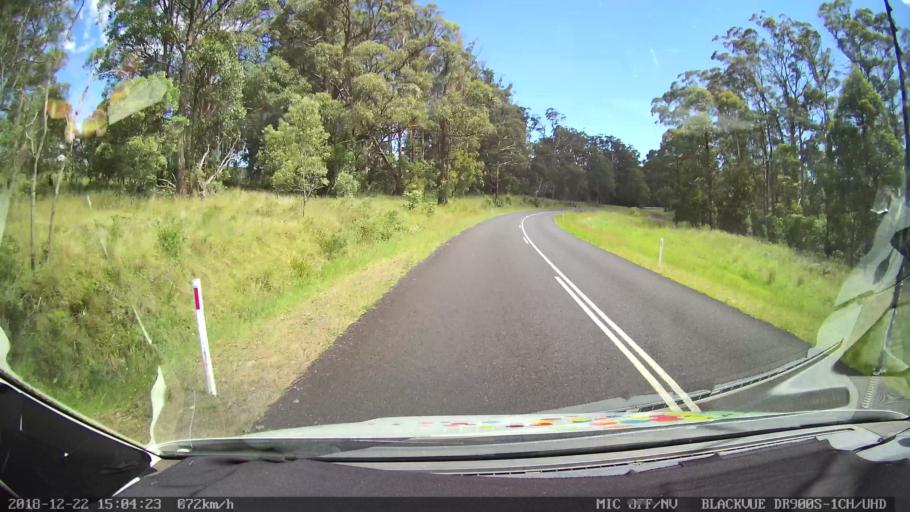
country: AU
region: New South Wales
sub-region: Bellingen
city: Dorrigo
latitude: -30.2742
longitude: 152.4383
